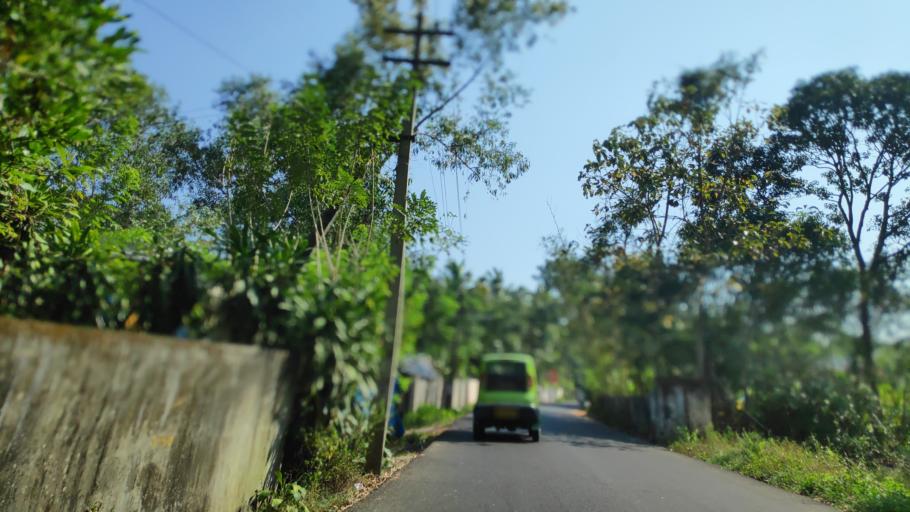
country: IN
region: Kerala
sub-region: Alappuzha
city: Alleppey
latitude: 9.5743
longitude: 76.3165
